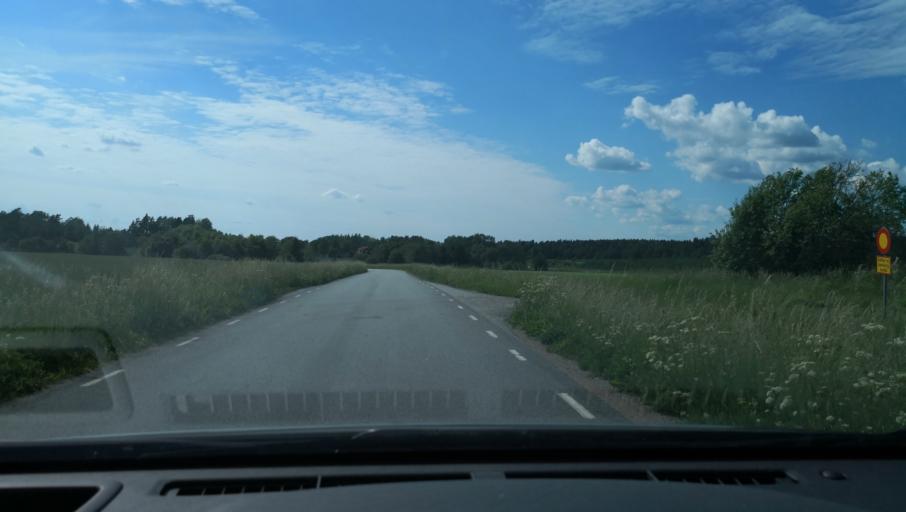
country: SE
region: Uppsala
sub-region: Enkopings Kommun
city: Orsundsbro
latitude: 59.8141
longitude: 17.3742
